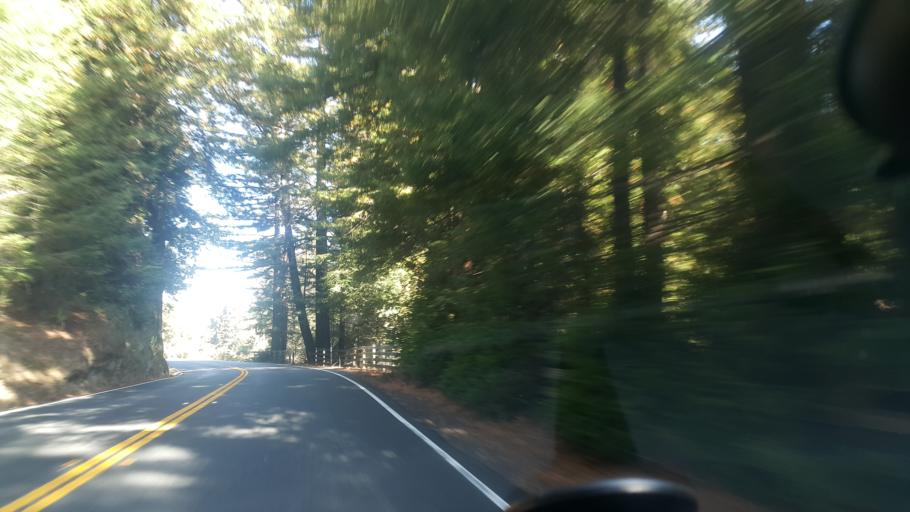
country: US
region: California
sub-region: Mendocino County
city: Fort Bragg
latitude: 39.3526
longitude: -123.6083
